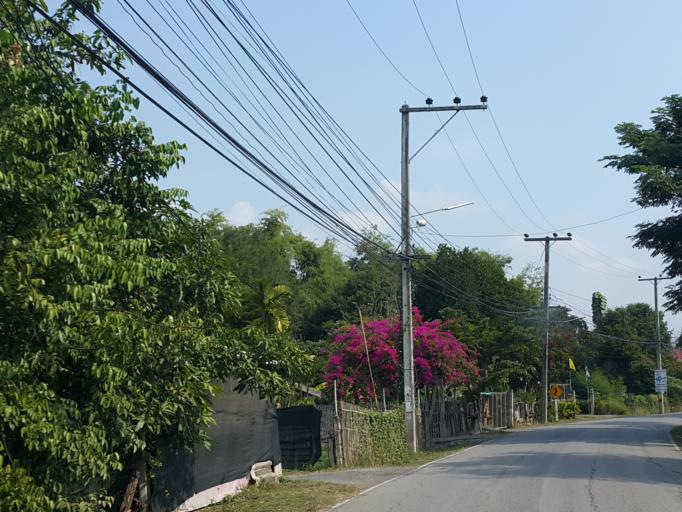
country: TH
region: Chiang Mai
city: San Kamphaeng
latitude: 18.8151
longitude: 99.1566
